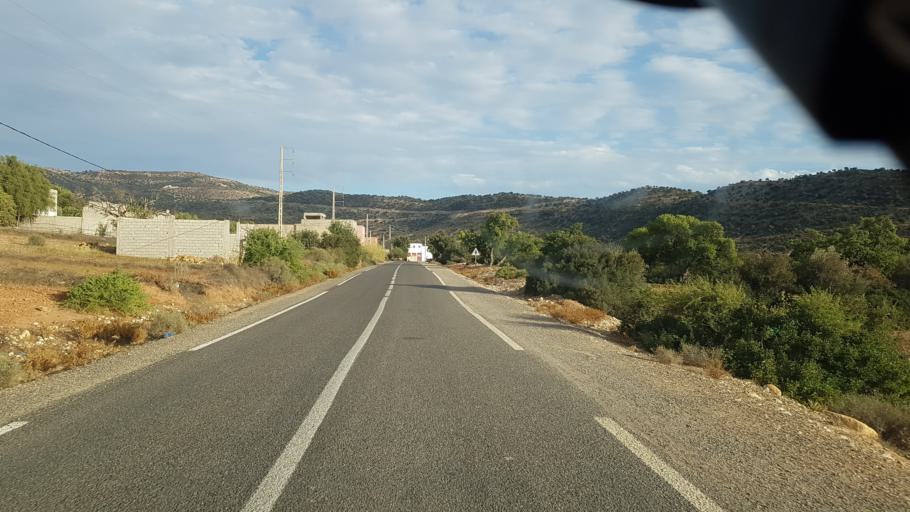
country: MA
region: Souss-Massa-Draa
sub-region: Agadir-Ida-ou-Tnan
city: Aourir
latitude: 30.5144
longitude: -9.5923
